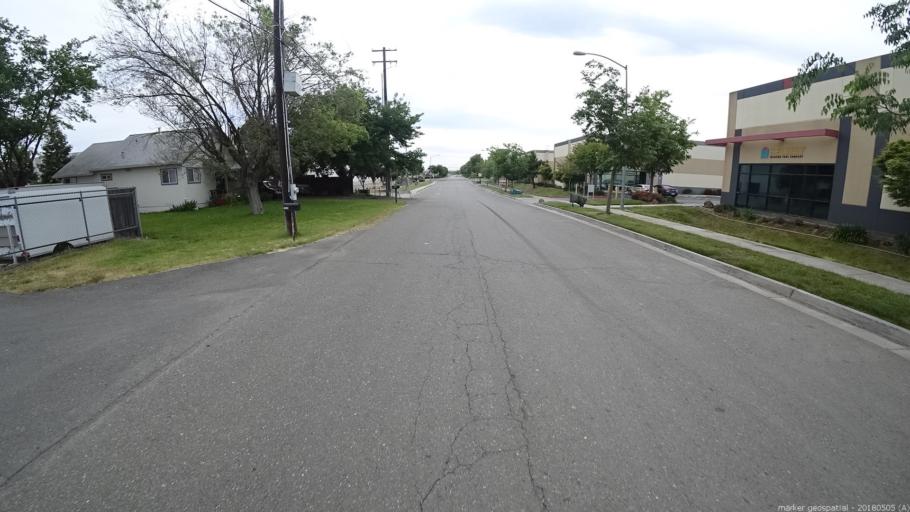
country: US
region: California
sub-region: Sacramento County
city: Rio Linda
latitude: 38.6583
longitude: -121.4311
